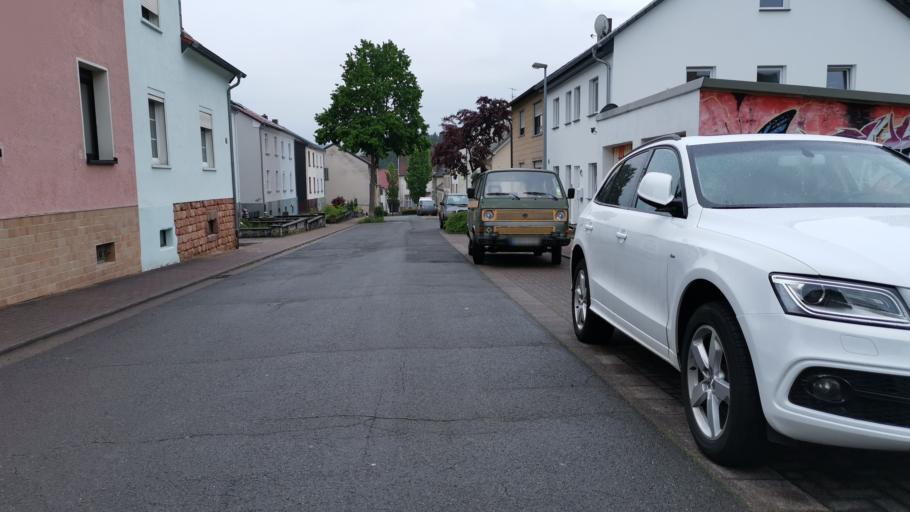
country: DE
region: Saarland
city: Sankt Ingbert
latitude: 49.2651
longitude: 7.1711
